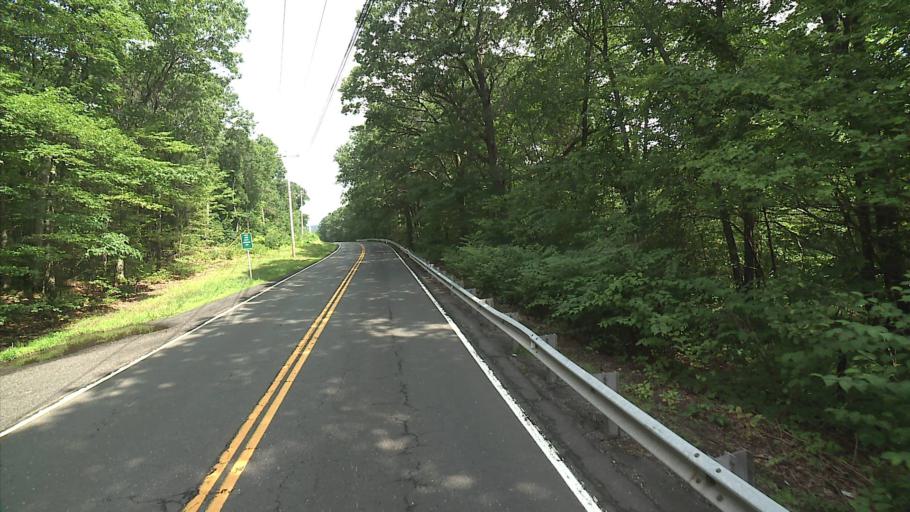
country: US
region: Connecticut
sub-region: New Haven County
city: Wolcott
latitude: 41.5856
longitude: -72.9535
